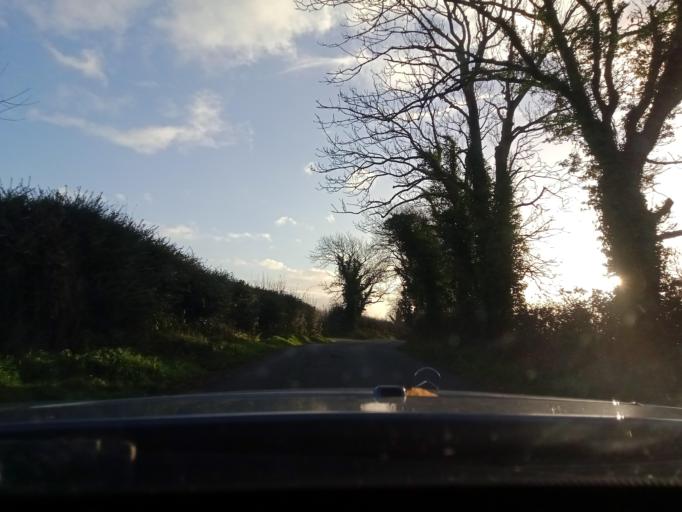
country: IE
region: Leinster
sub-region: Kilkenny
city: Callan
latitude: 52.5334
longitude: -7.3779
